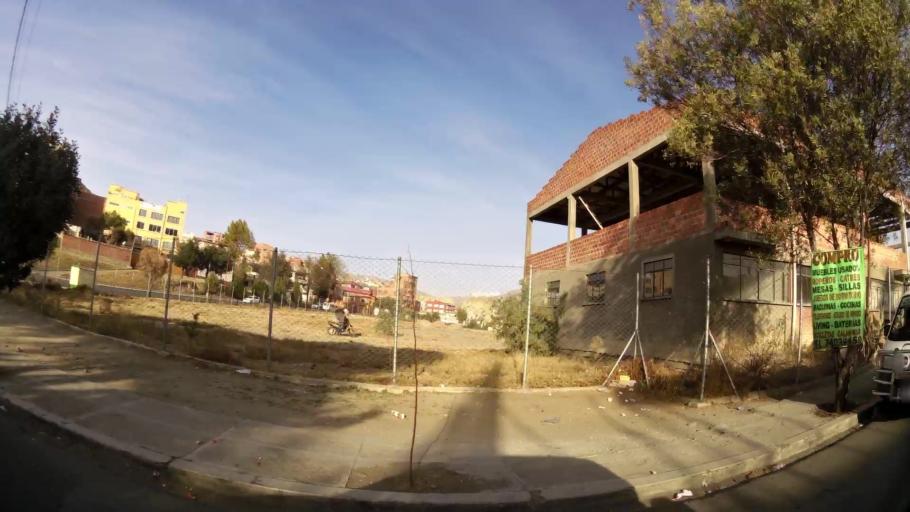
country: BO
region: La Paz
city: La Paz
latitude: -16.5230
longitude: -68.1043
